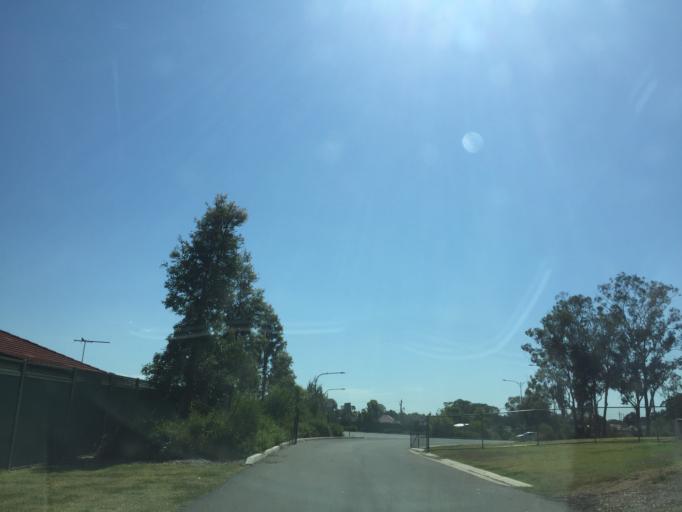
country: AU
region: New South Wales
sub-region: Blacktown
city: Blacktown
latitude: -33.7648
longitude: 150.8997
